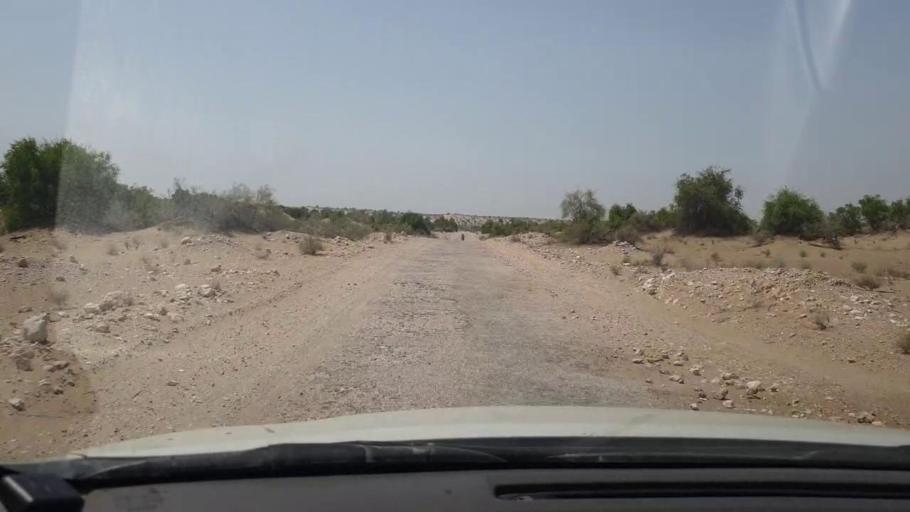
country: PK
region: Sindh
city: Rohri
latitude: 27.3134
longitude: 69.2817
